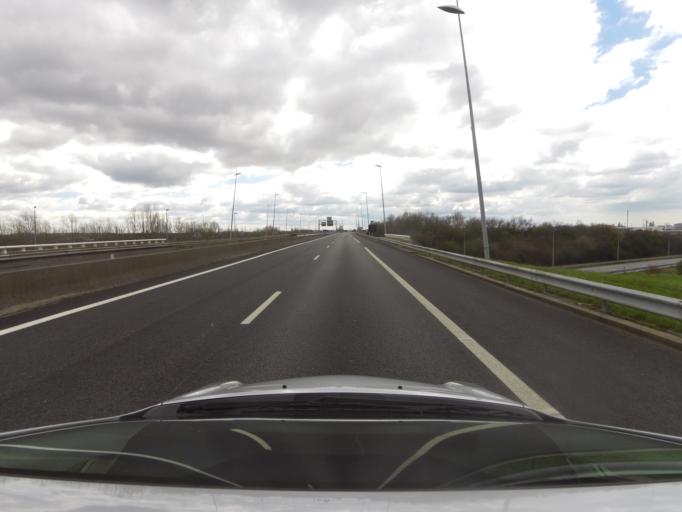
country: FR
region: Haute-Normandie
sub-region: Departement de la Seine-Maritime
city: Rogerville
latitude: 49.4938
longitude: 0.2660
